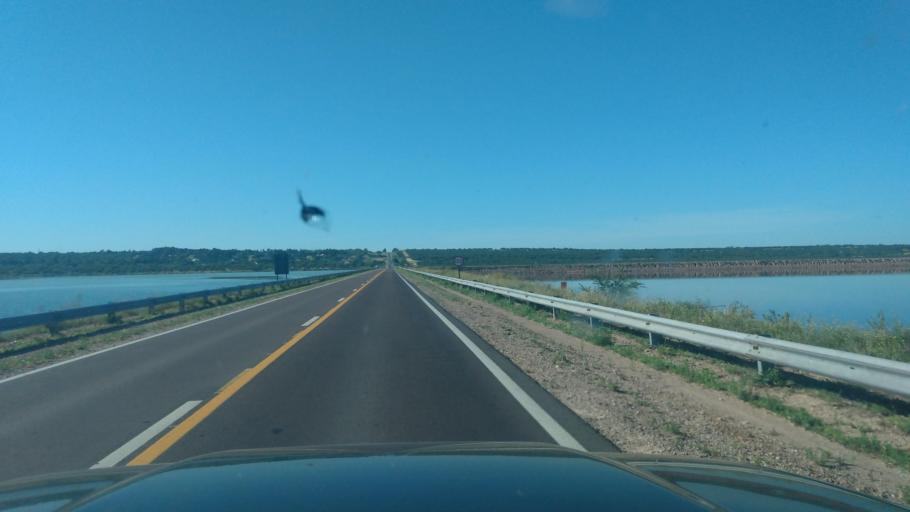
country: AR
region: La Pampa
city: Santa Rosa
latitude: -36.7106
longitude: -64.2831
